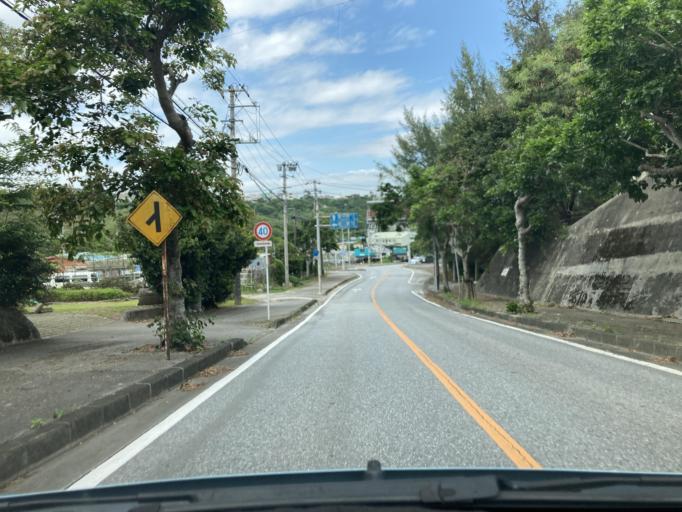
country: JP
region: Okinawa
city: Ginowan
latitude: 26.2717
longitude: 127.7810
